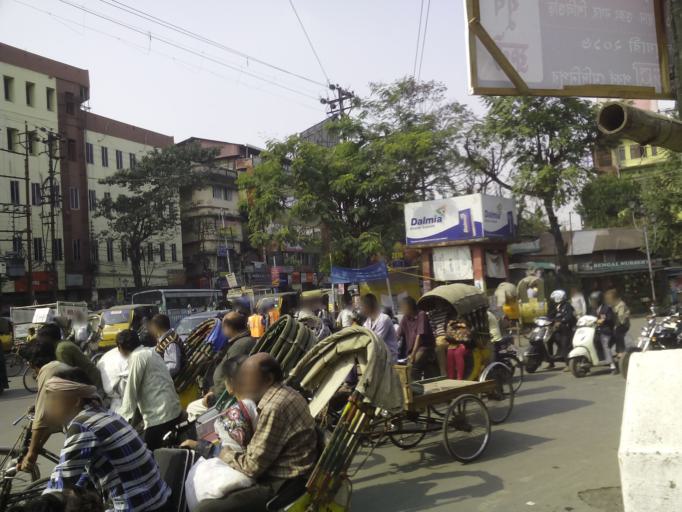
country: IN
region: West Bengal
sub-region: Darjiling
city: Shiliguri
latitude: 26.7113
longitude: 88.4262
